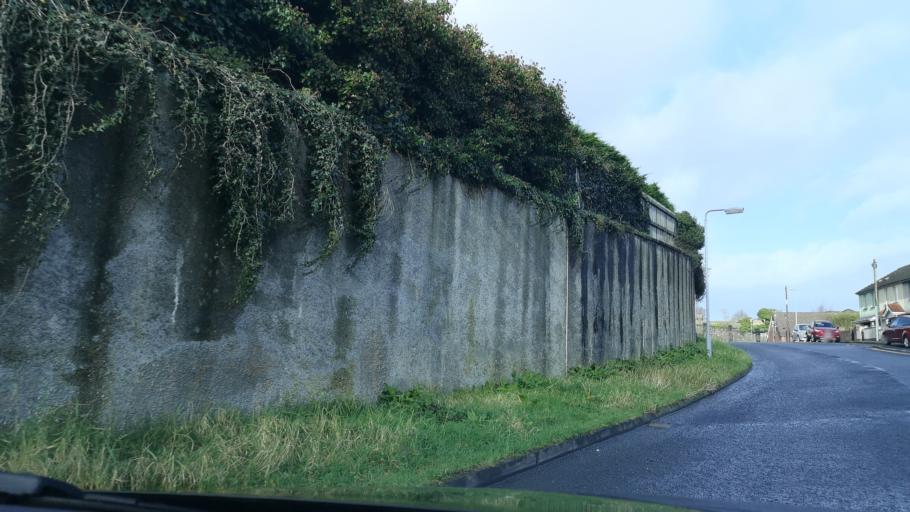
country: GB
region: Northern Ireland
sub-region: Newry and Mourne District
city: Newry
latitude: 54.1770
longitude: -6.3488
